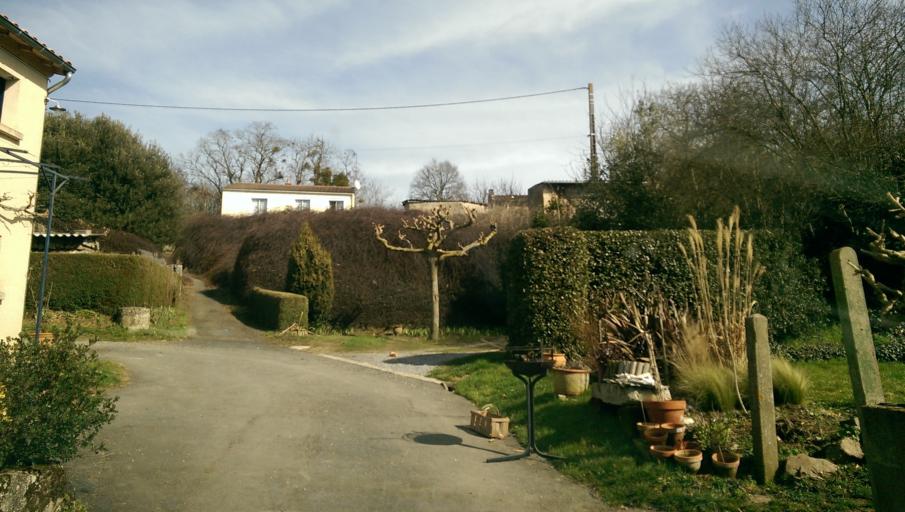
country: FR
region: Pays de la Loire
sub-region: Departement de Maine-et-Loire
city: Nueil-sur-Layon
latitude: 47.1756
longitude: -0.3407
